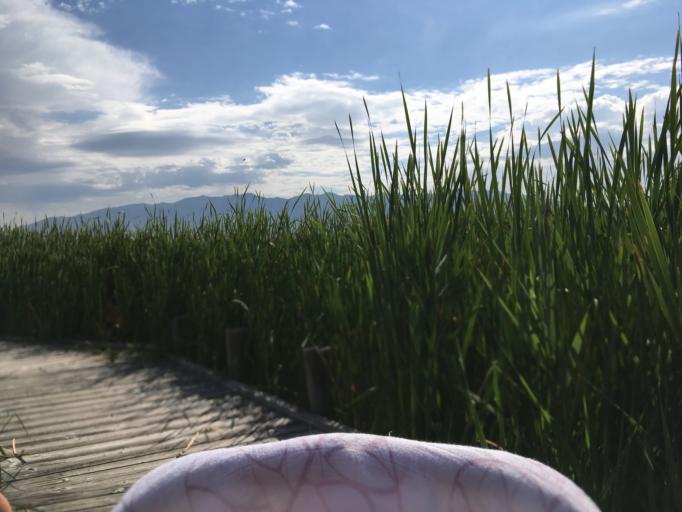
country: US
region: Utah
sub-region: Davis County
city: Syracuse
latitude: 41.0391
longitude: -112.0290
